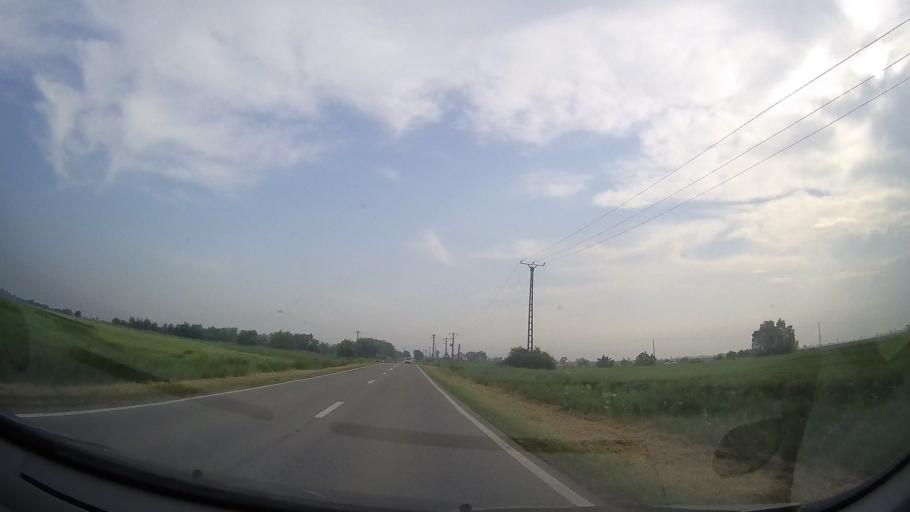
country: RO
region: Timis
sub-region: Comuna Parta
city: Parta
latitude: 45.6573
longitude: 21.1470
